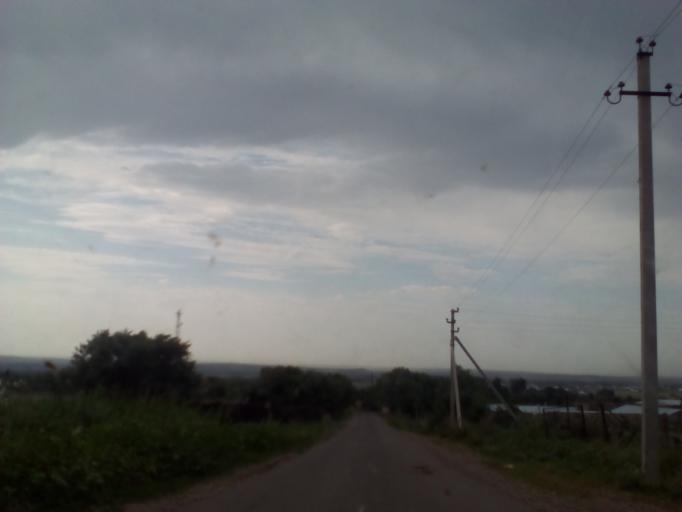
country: KZ
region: Almaty Oblysy
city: Burunday
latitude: 43.1550
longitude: 76.3850
